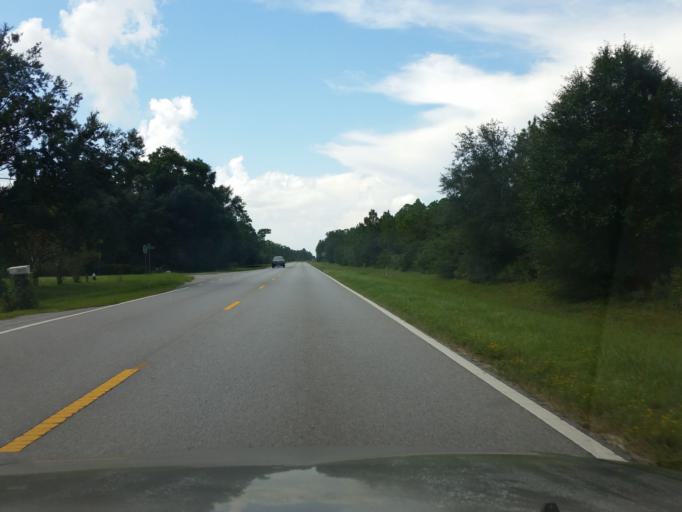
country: US
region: Florida
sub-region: Escambia County
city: Myrtle Grove
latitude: 30.3792
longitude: -87.4022
